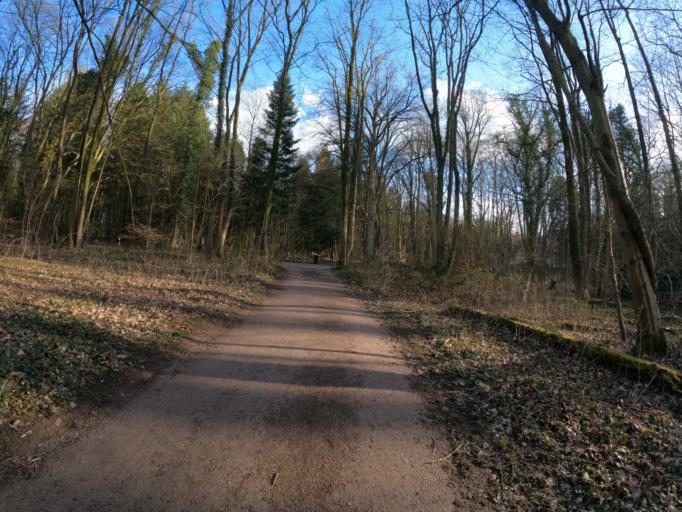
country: DE
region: Hamburg
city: Stellingen
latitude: 53.6166
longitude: 9.9364
